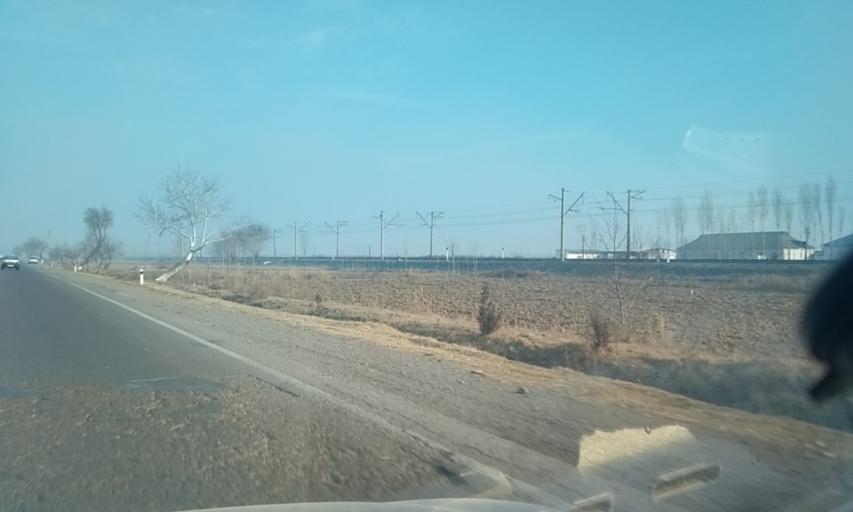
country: UZ
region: Sirdaryo
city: Sirdaryo
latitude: 40.7758
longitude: 68.6815
